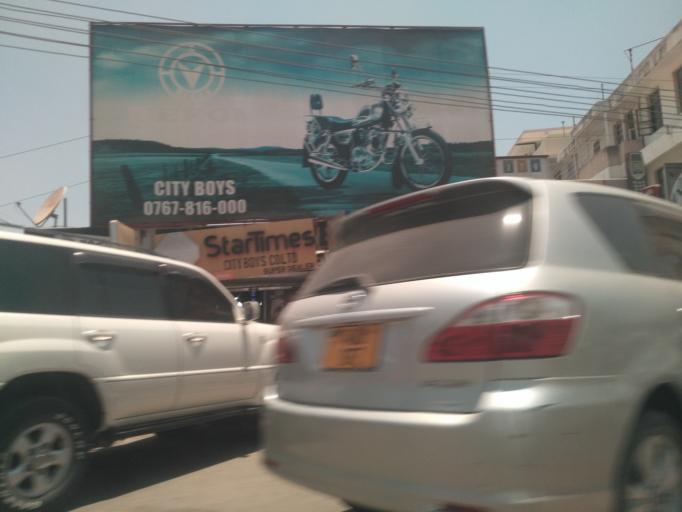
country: TZ
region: Dodoma
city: Dodoma
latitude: -6.1789
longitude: 35.7432
